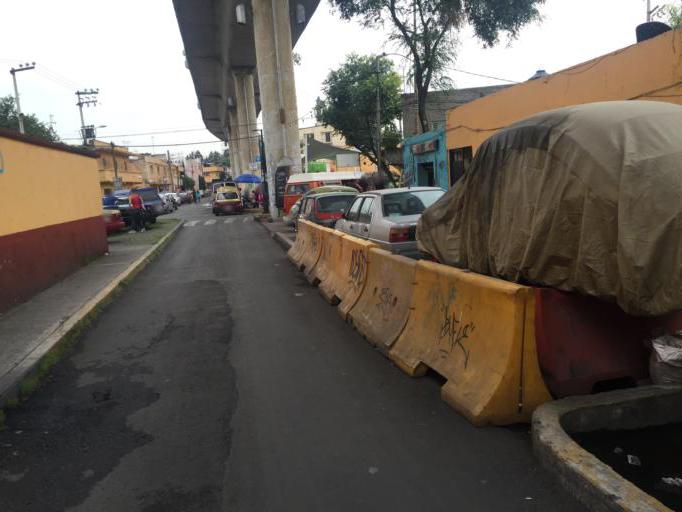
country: MX
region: Mexico City
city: Alvaro Obregon
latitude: 19.3789
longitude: -99.1931
